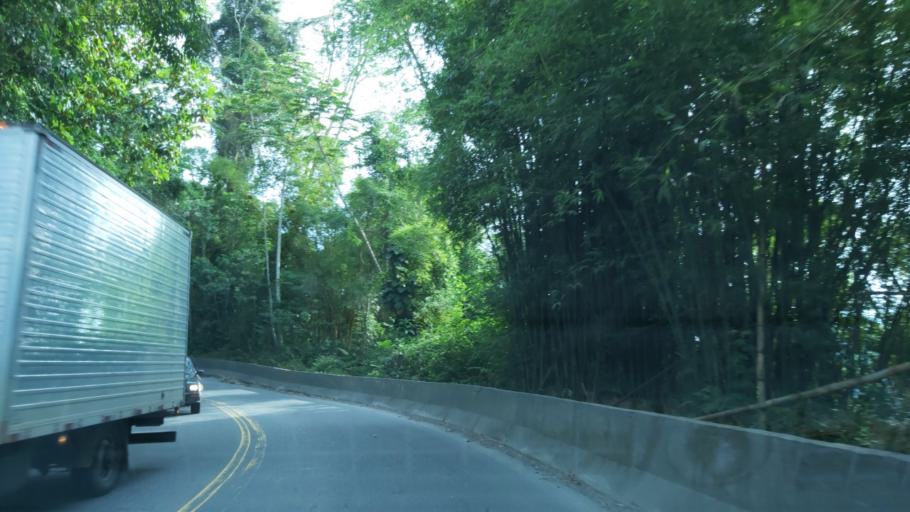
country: BR
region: Sao Paulo
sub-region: Juquia
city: Juquia
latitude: -24.1102
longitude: -47.6268
